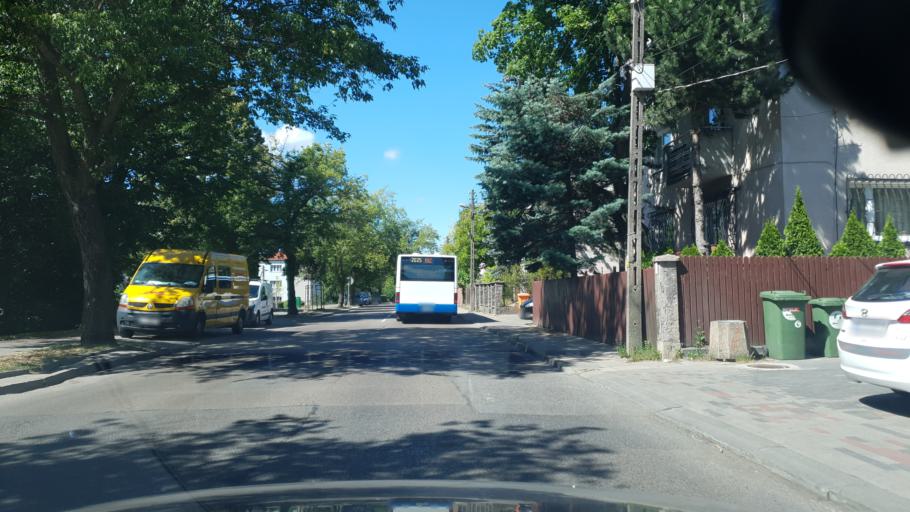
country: PL
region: Pomeranian Voivodeship
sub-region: Gdynia
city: Gdynia
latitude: 54.5005
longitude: 18.5414
